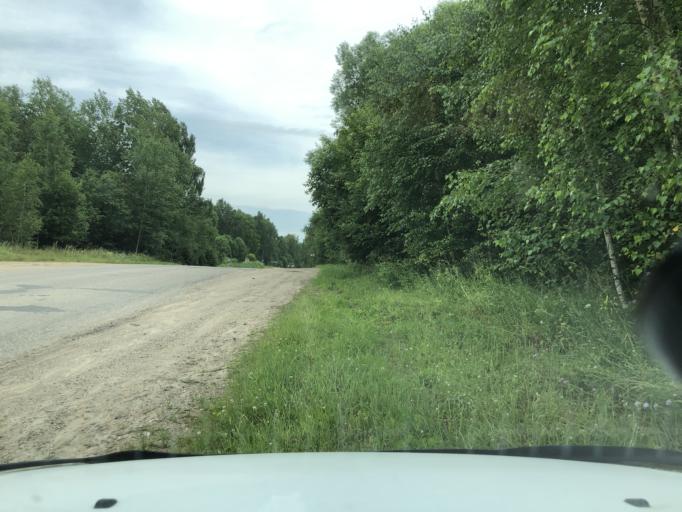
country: RU
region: Jaroslavl
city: Petrovsk
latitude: 56.9861
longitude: 39.1532
